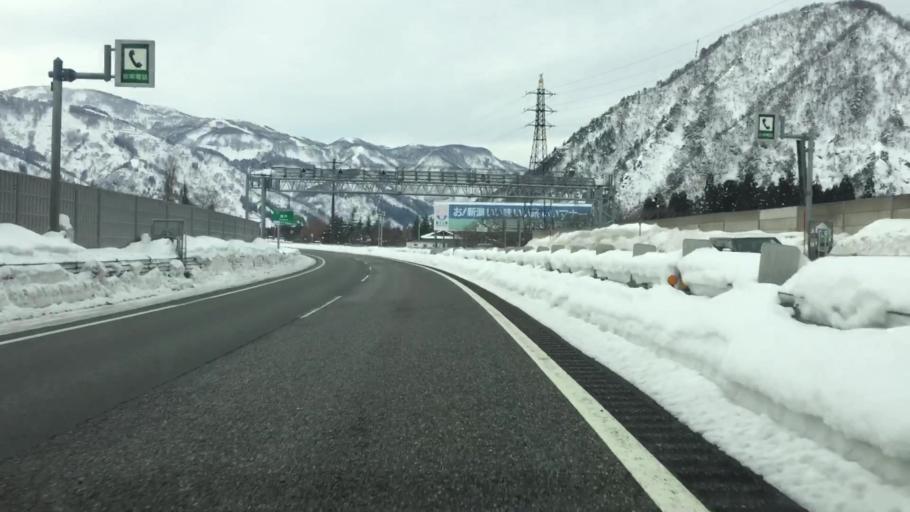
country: JP
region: Niigata
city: Shiozawa
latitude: 36.9288
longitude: 138.8382
